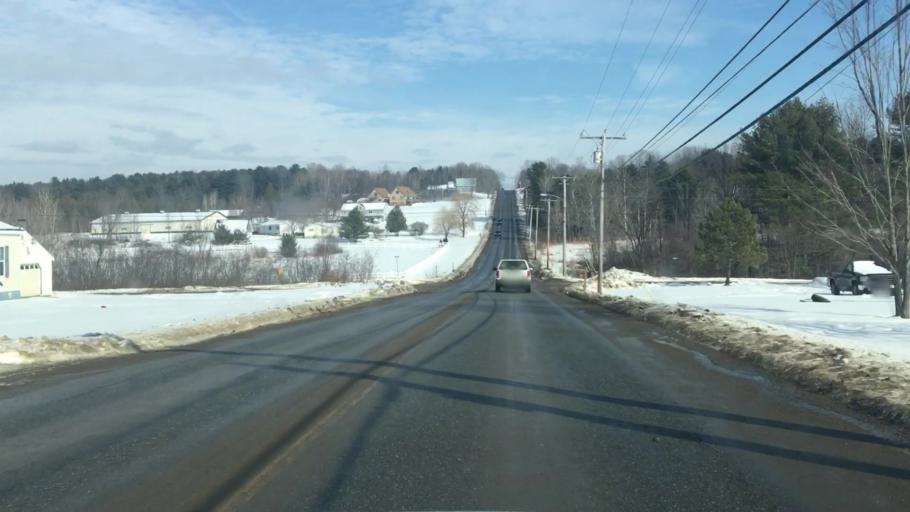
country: US
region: Maine
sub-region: Penobscot County
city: Hermon
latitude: 44.8296
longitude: -68.8843
